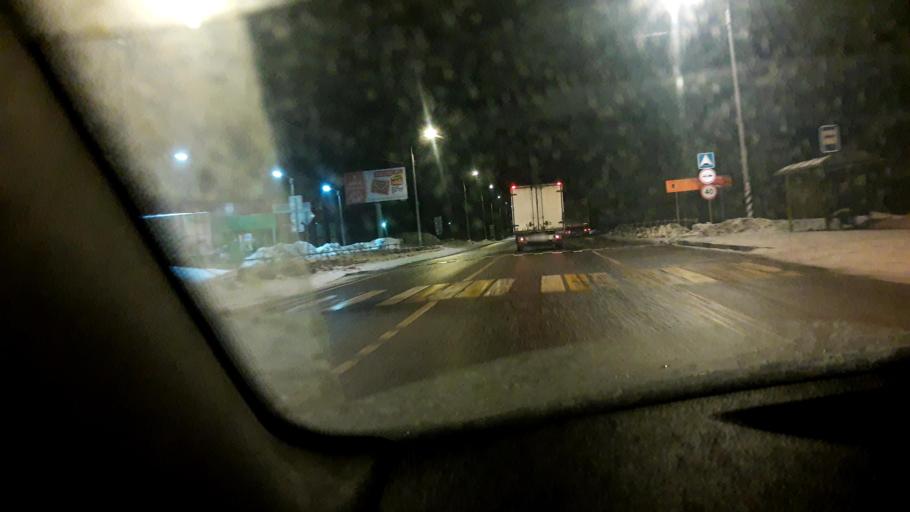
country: RU
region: Moskovskaya
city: Skoropuskovskiy
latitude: 56.3816
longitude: 38.1070
